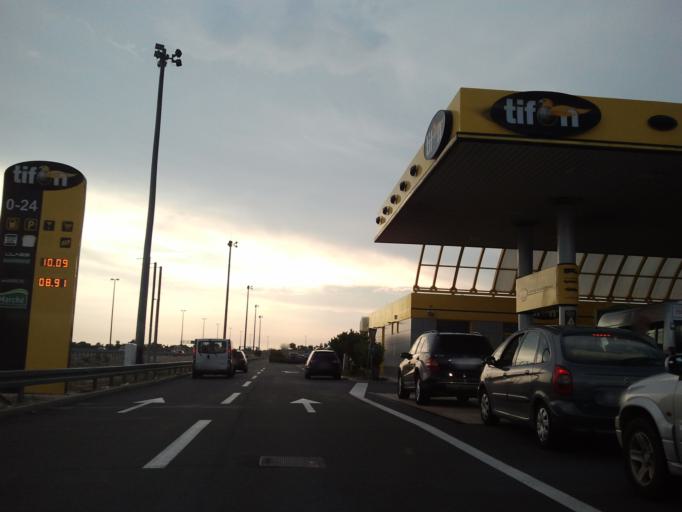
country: HR
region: Zadarska
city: Pridraga
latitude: 44.2407
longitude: 15.5685
